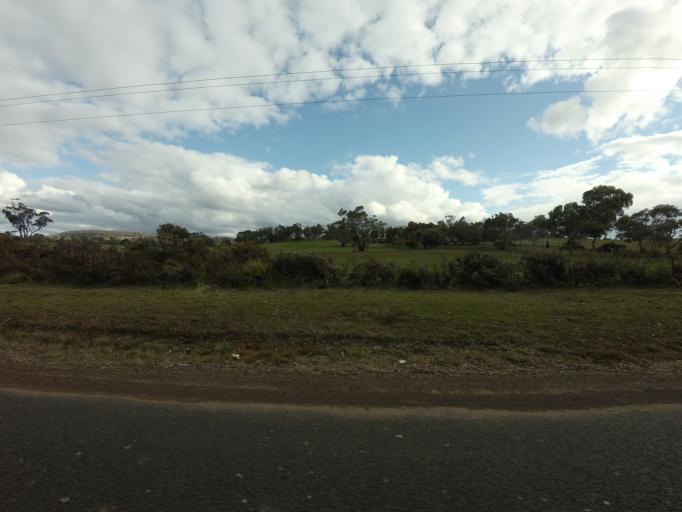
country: AU
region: Tasmania
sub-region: Northern Midlands
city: Evandale
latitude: -41.8742
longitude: 147.3017
